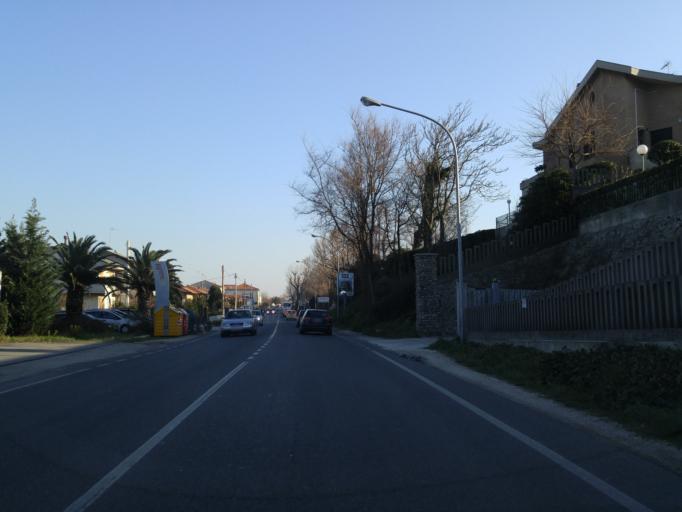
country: IT
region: The Marches
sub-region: Provincia di Pesaro e Urbino
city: Fano
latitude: 43.8546
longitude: 13.0022
